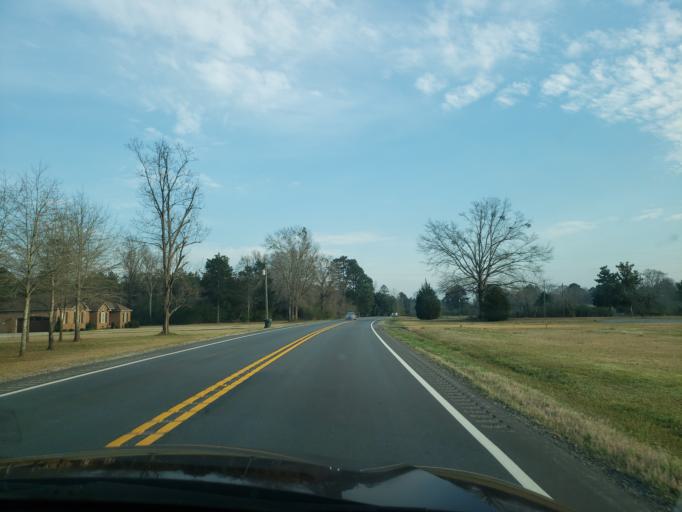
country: US
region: Alabama
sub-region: Hale County
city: Moundville
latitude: 32.8881
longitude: -87.6099
